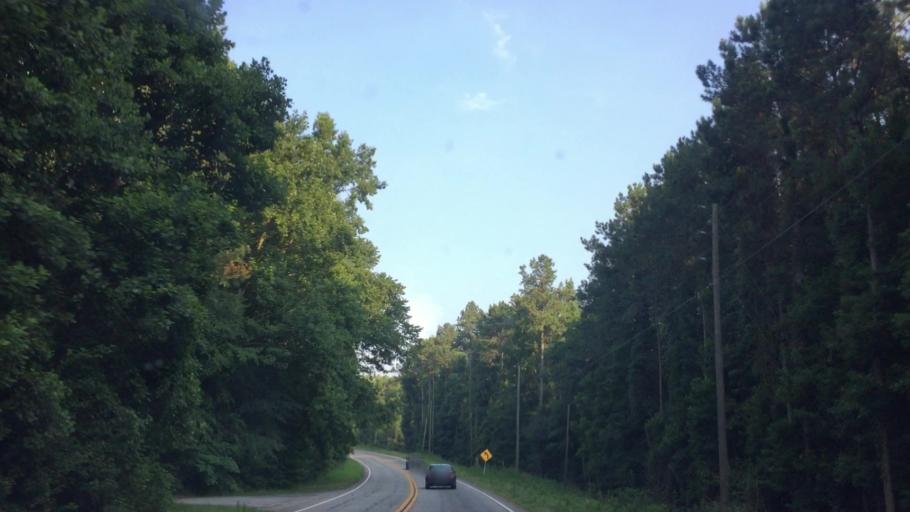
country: US
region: Georgia
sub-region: DeKalb County
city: Pine Mountain
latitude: 33.6296
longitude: -84.1819
